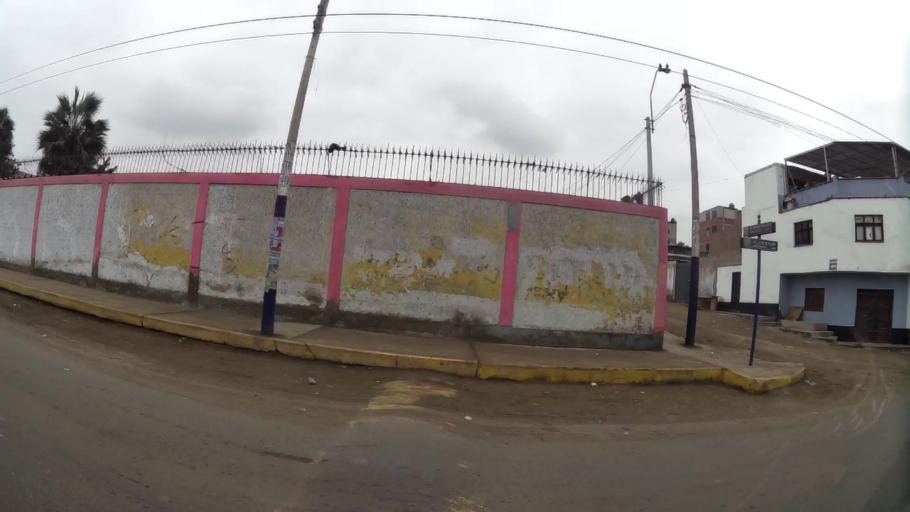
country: PE
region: Lima
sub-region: Lima
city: Surco
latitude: -12.2002
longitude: -76.9930
